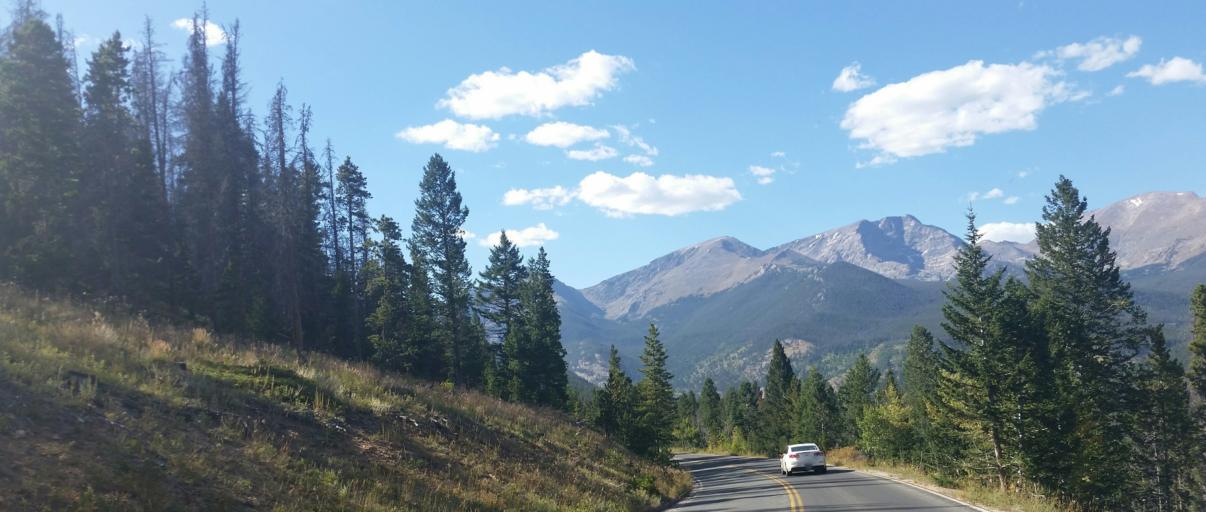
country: US
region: Colorado
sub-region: Larimer County
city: Estes Park
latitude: 40.3902
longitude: -105.6200
